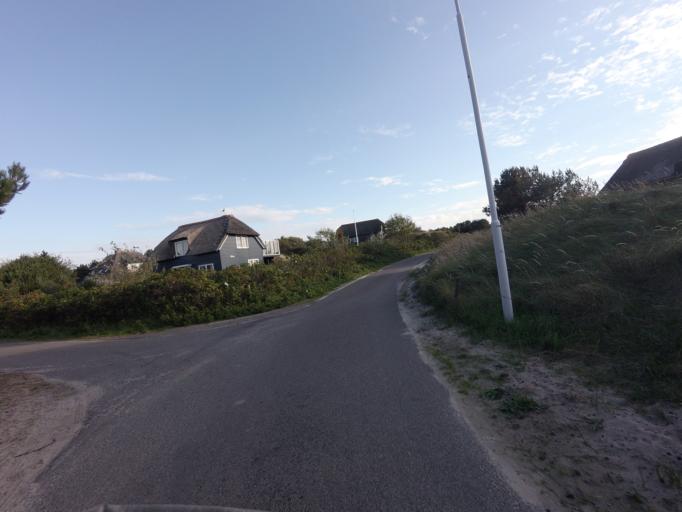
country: NL
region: Friesland
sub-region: Gemeente Ameland
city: Nes
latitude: 53.4577
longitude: 5.8019
